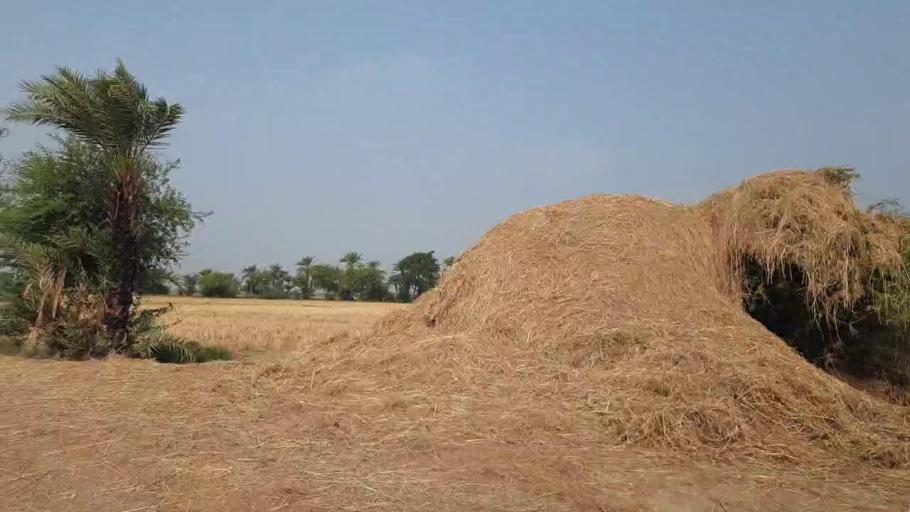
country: PK
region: Sindh
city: Kario
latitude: 24.7588
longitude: 68.5478
